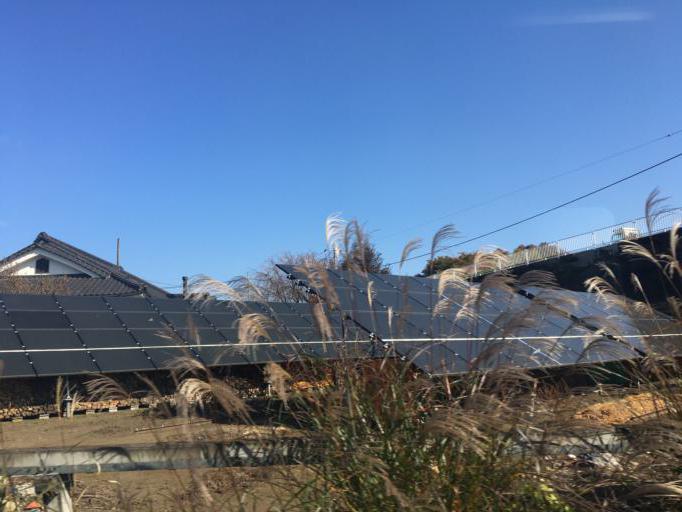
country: JP
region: Tochigi
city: Oyama
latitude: 36.3313
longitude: 139.8075
